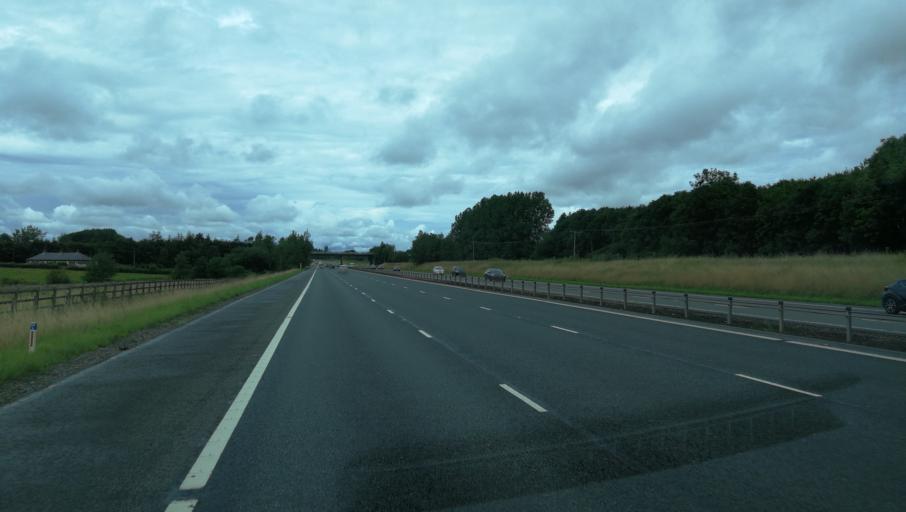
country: GB
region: Scotland
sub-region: Dumfries and Galloway
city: Lockerbie
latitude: 55.1574
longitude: -3.3852
